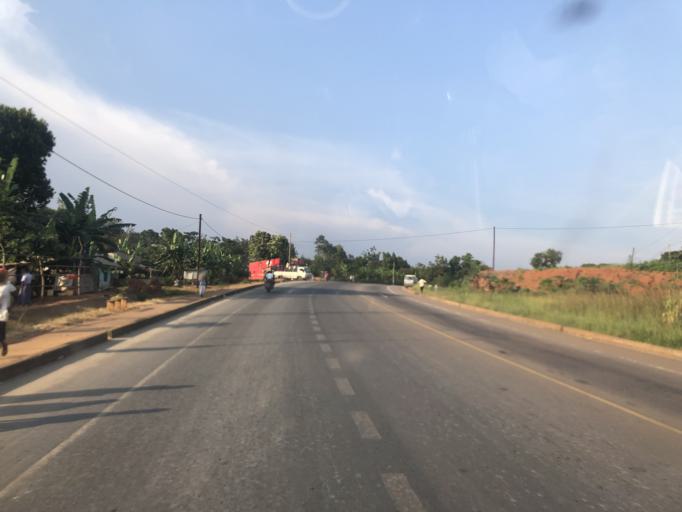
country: UG
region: Central Region
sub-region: Mpigi District
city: Mpigi
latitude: 0.1708
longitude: 32.2609
